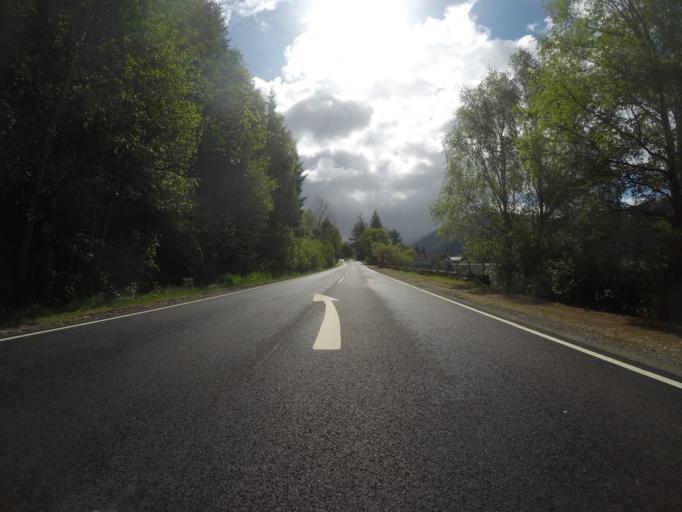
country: GB
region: Scotland
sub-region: Highland
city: Fort William
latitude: 57.2445
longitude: -5.4619
